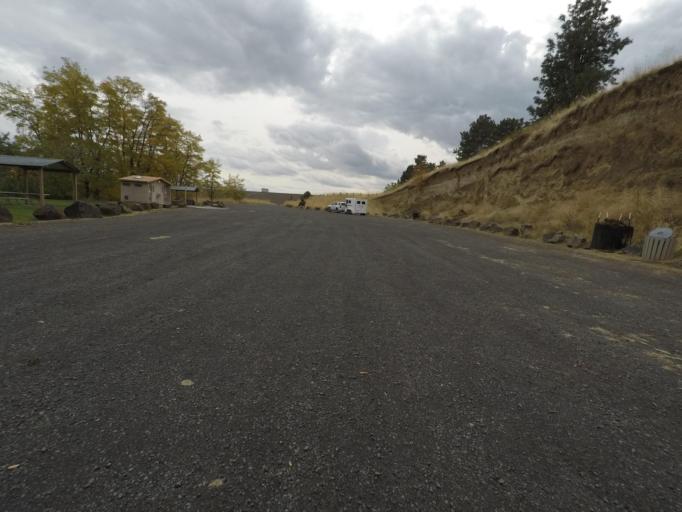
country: US
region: Washington
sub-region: Walla Walla County
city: Walla Walla East
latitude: 46.0671
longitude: -118.2643
